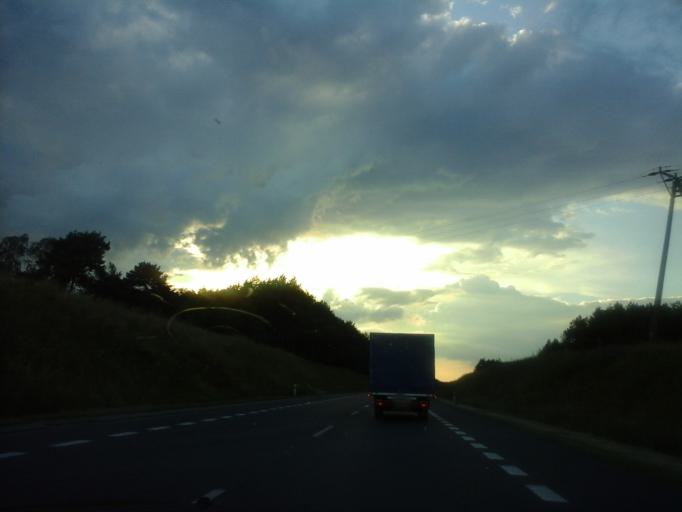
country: PL
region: Lubusz
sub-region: Powiat nowosolski
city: Nowa Sol
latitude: 51.7588
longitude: 15.6870
